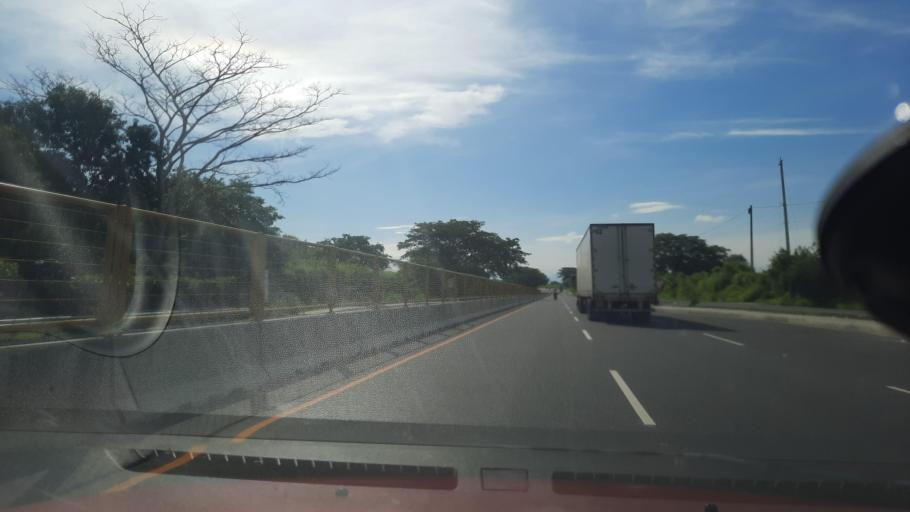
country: SV
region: La Paz
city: El Rosario
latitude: 13.4861
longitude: -88.9909
